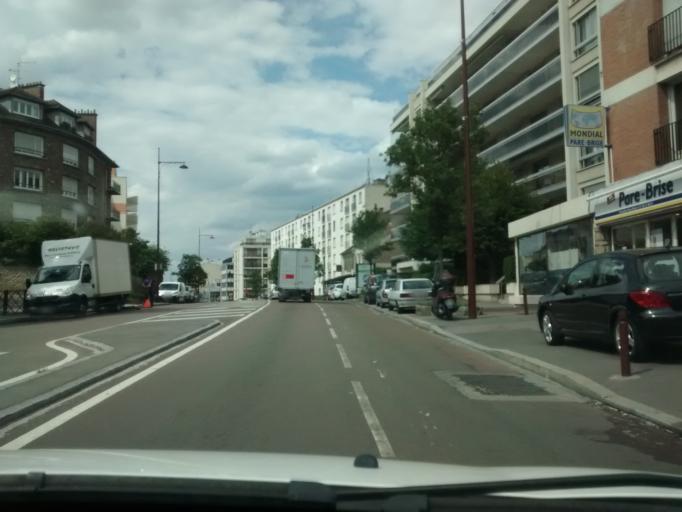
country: FR
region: Ile-de-France
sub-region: Departement des Yvelines
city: Versailles
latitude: 48.7906
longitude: 2.1475
